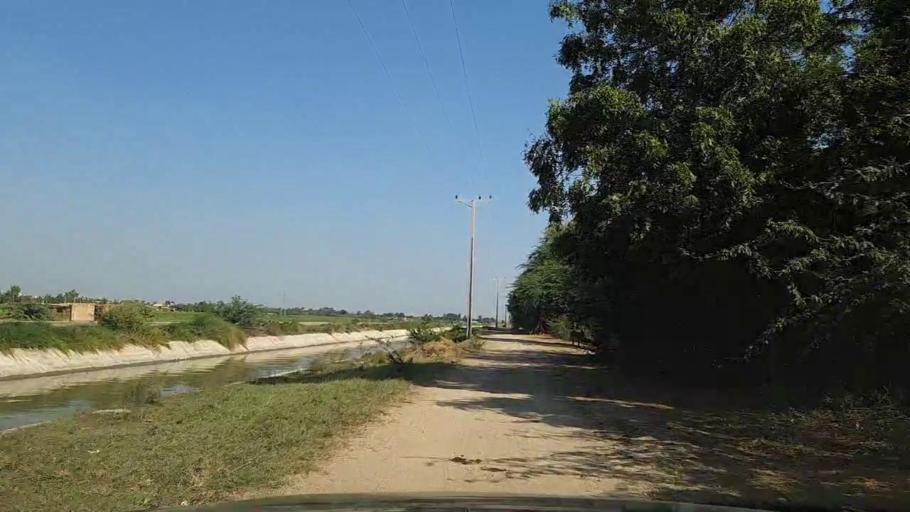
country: PK
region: Sindh
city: Mirpur Sakro
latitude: 24.5966
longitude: 67.8091
